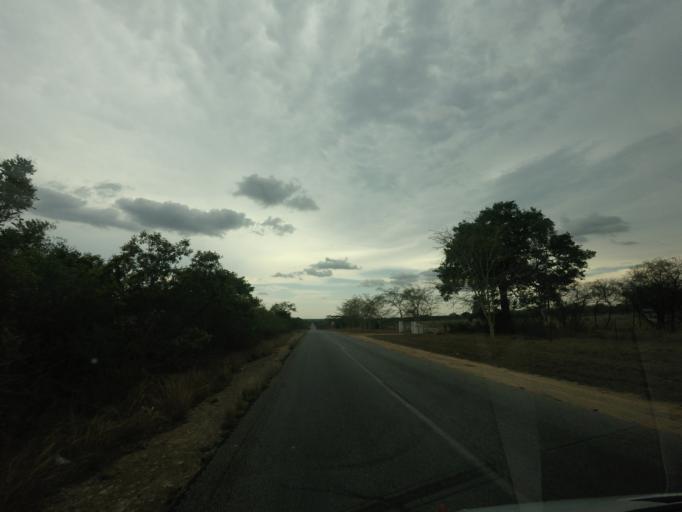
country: ZA
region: Limpopo
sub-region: Mopani District Municipality
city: Hoedspruit
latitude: -24.5278
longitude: 30.9693
